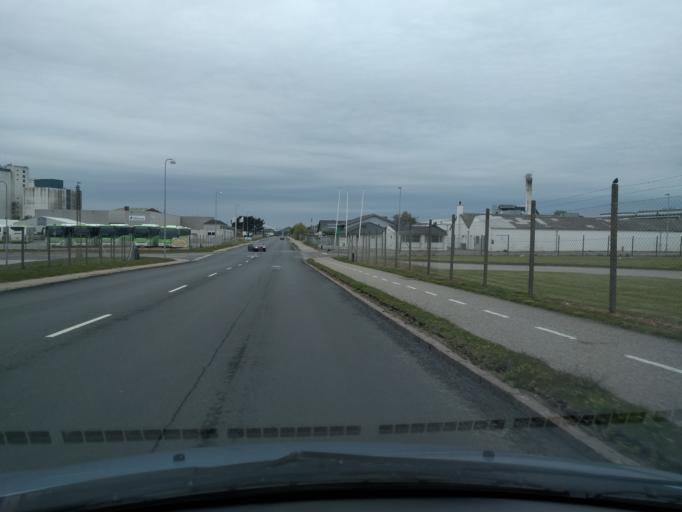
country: DK
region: South Denmark
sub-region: Odense Kommune
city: Odense
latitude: 55.4140
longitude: 10.3846
